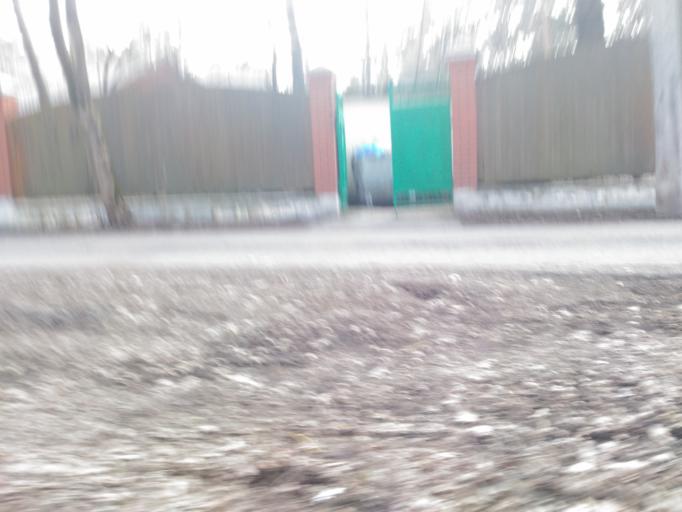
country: RU
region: Moscow
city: Strogino
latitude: 55.7841
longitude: 37.4105
